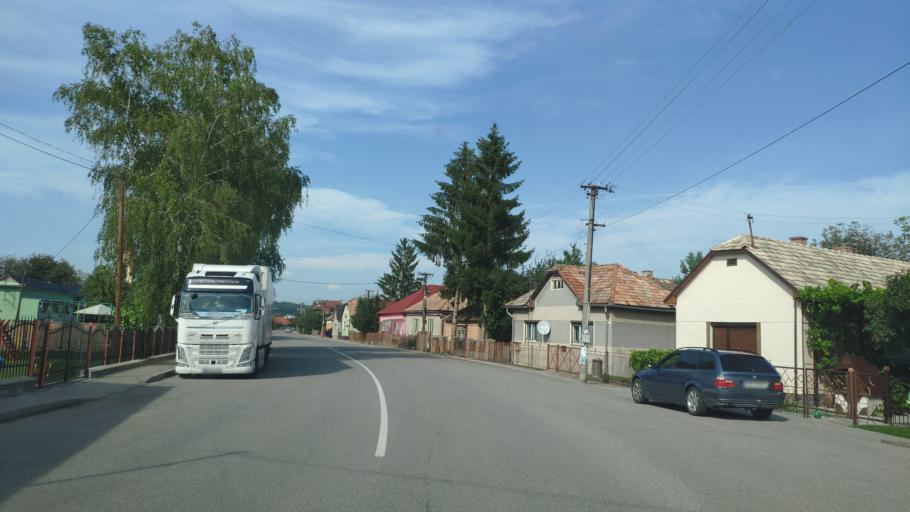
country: HU
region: Borsod-Abauj-Zemplen
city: Putnok
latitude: 48.4722
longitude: 20.3507
